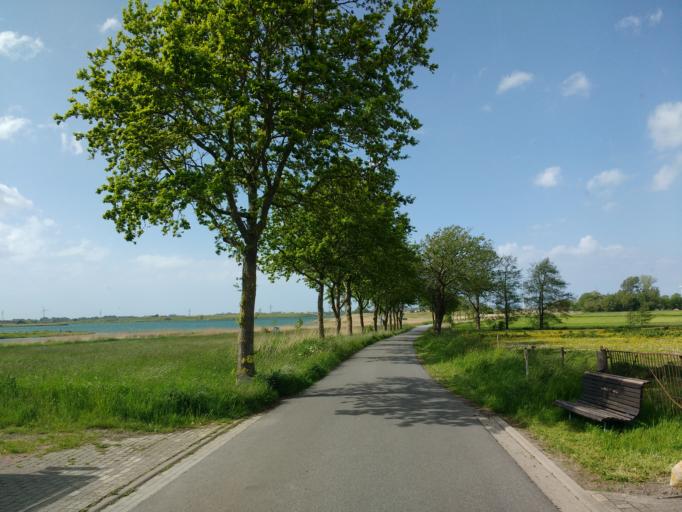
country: DE
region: Lower Saxony
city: Jever
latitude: 53.6668
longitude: 7.9296
